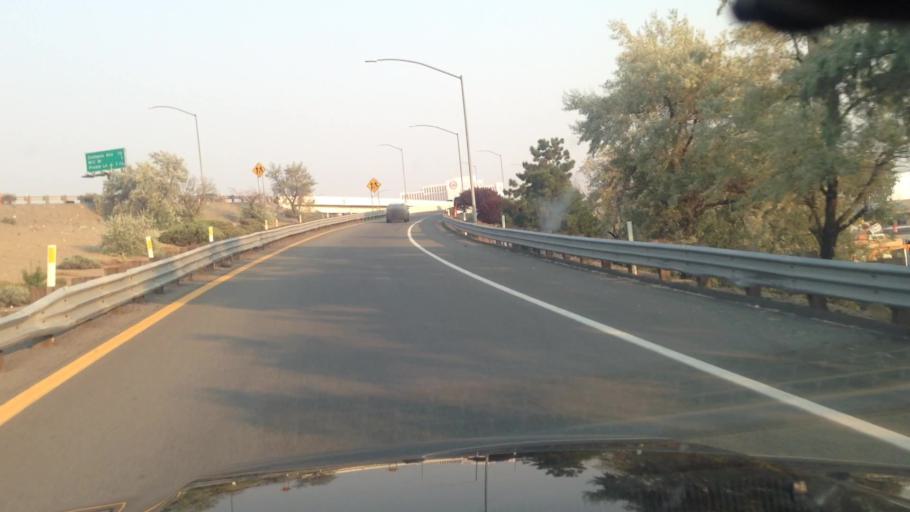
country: US
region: Nevada
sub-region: Washoe County
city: Reno
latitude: 39.5349
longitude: -119.7889
